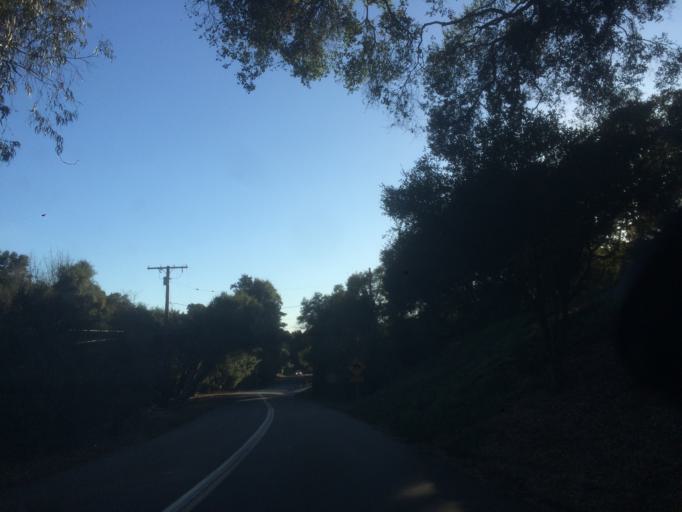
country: US
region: California
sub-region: Santa Barbara County
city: Goleta
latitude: 34.4207
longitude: -119.7722
